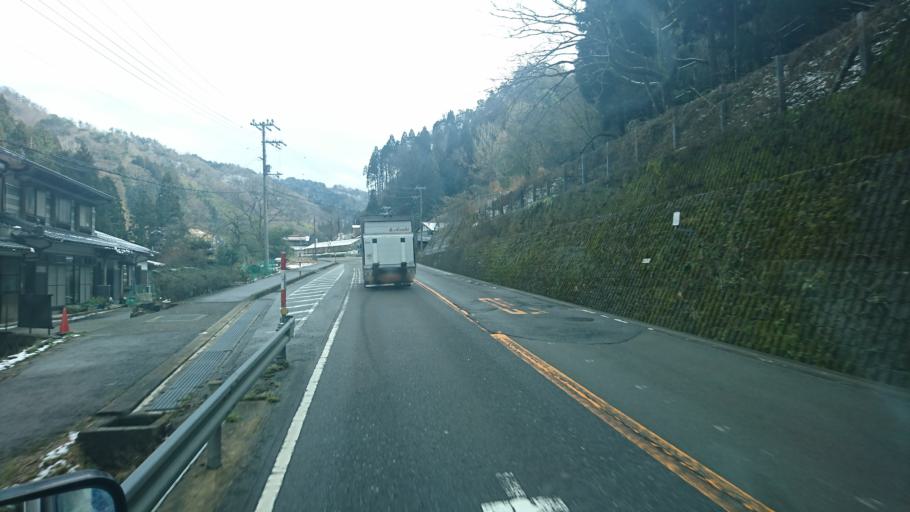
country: JP
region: Tottori
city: Tottori
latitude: 35.5261
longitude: 134.5187
